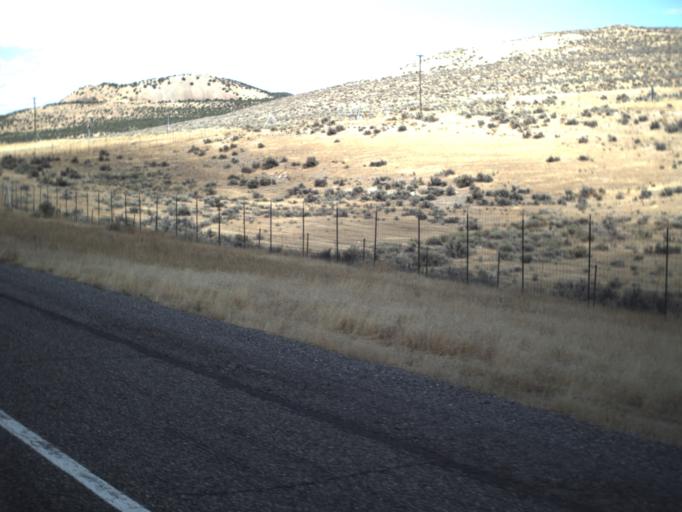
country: US
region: Idaho
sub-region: Oneida County
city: Malad City
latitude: 41.9637
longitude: -112.7523
